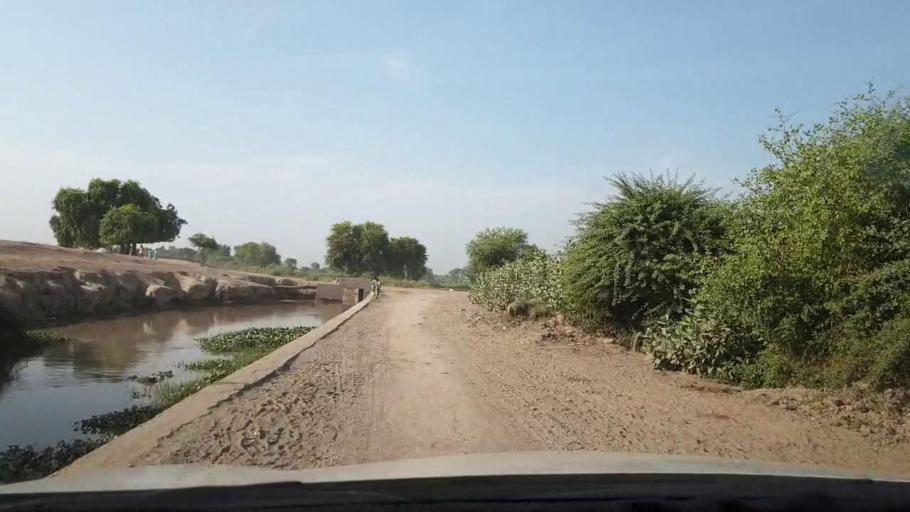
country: PK
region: Sindh
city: Larkana
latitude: 27.5457
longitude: 68.2672
